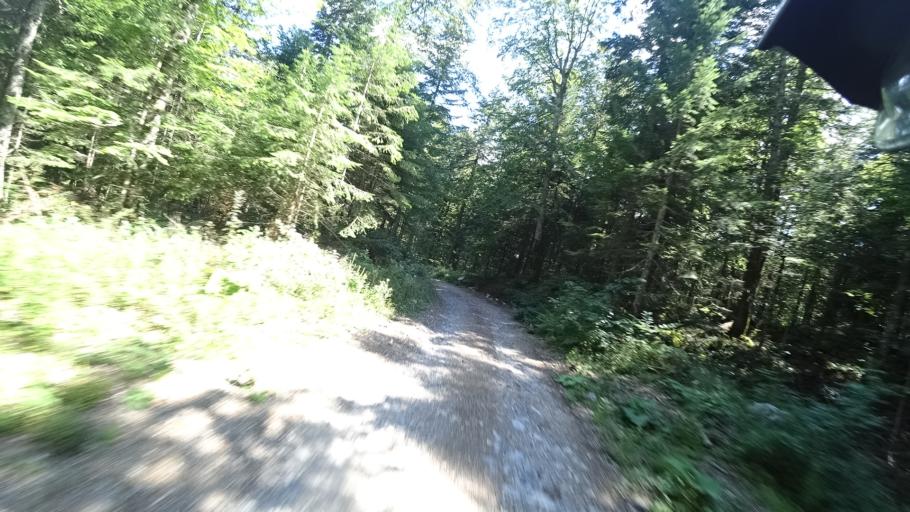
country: BA
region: Federation of Bosnia and Herzegovina
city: Orasac
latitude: 44.5066
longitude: 15.9286
